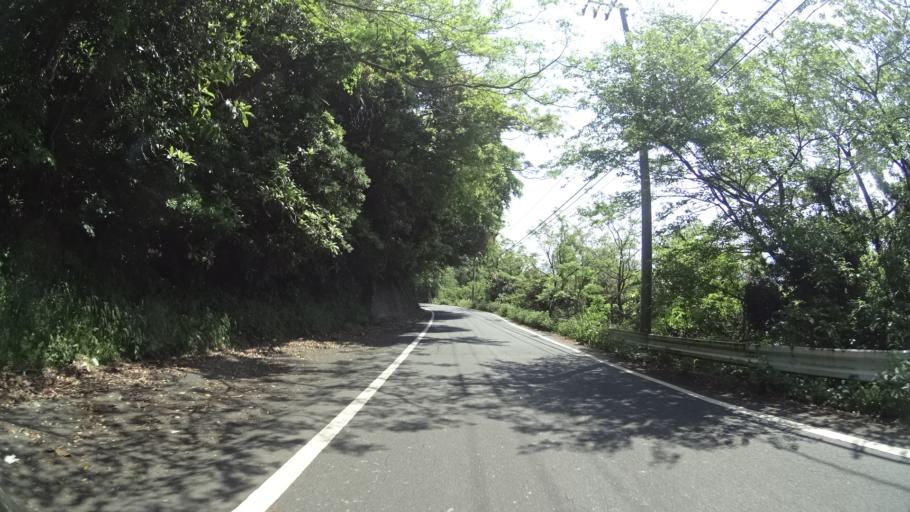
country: JP
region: Ehime
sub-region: Nishiuwa-gun
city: Ikata-cho
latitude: 33.3891
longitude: 132.0989
